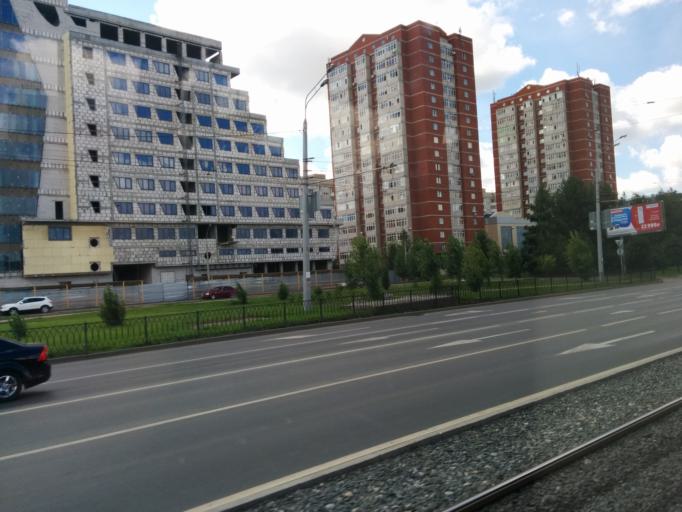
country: RU
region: Tatarstan
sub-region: Gorod Kazan'
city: Kazan
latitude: 55.8271
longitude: 49.1206
